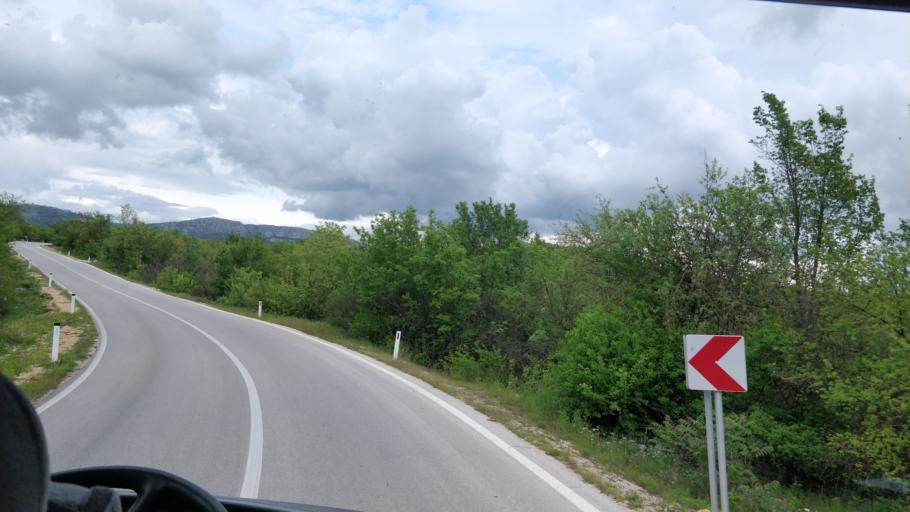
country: BA
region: Federation of Bosnia and Herzegovina
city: Ljubuski
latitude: 43.1760
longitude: 17.5048
